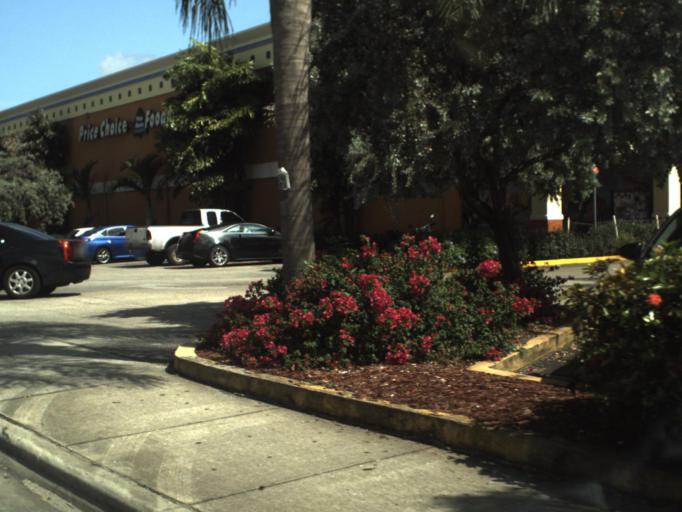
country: US
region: Florida
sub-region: Miami-Dade County
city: Carol City
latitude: 25.9397
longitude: -80.2755
